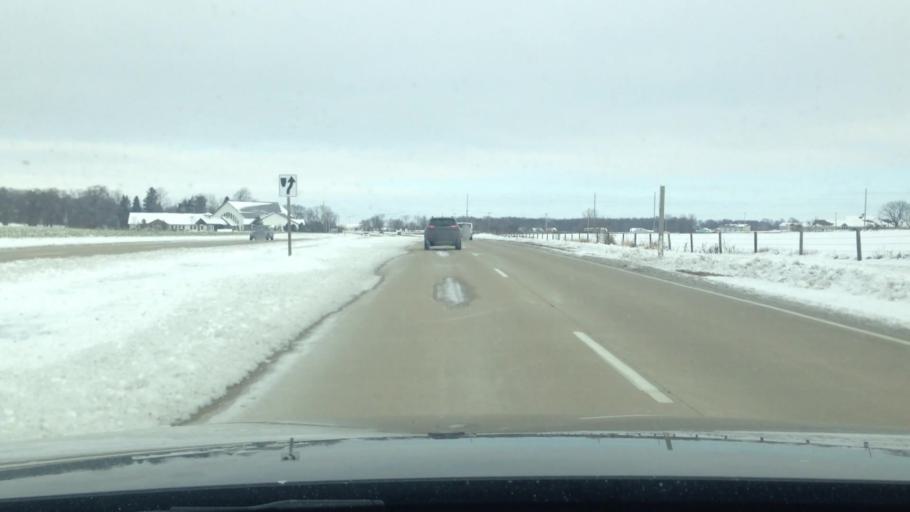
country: US
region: Wisconsin
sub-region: Walworth County
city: Lake Geneva
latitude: 42.5702
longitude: -88.4127
